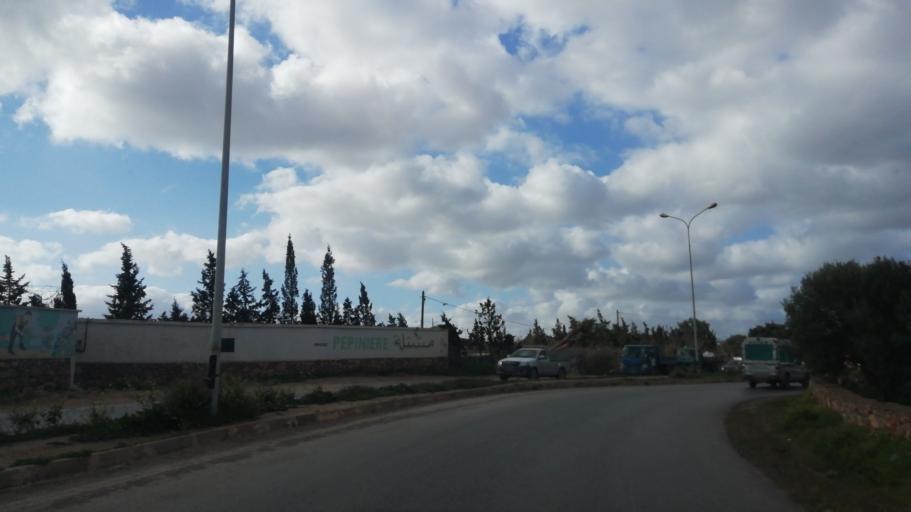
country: DZ
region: Oran
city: Es Senia
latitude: 35.6483
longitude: -0.6676
